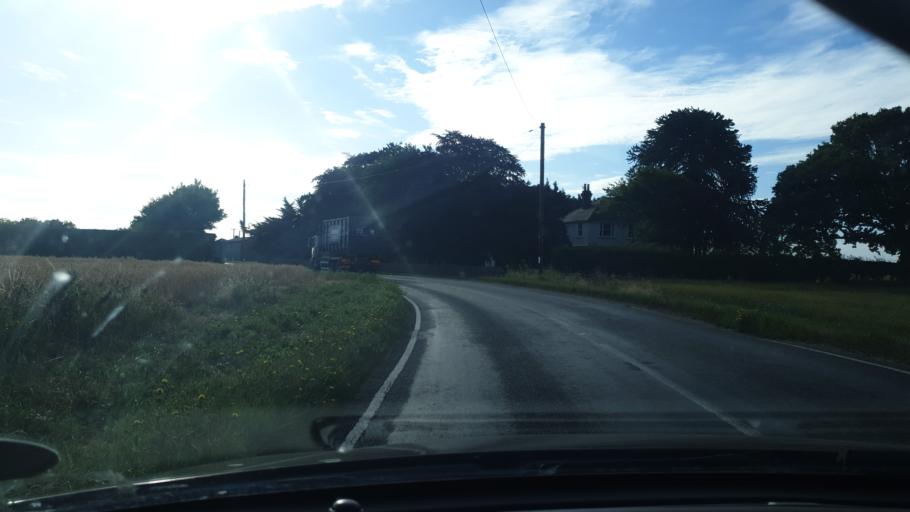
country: GB
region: England
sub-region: Essex
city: Frinton-on-Sea
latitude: 51.8526
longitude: 1.1984
